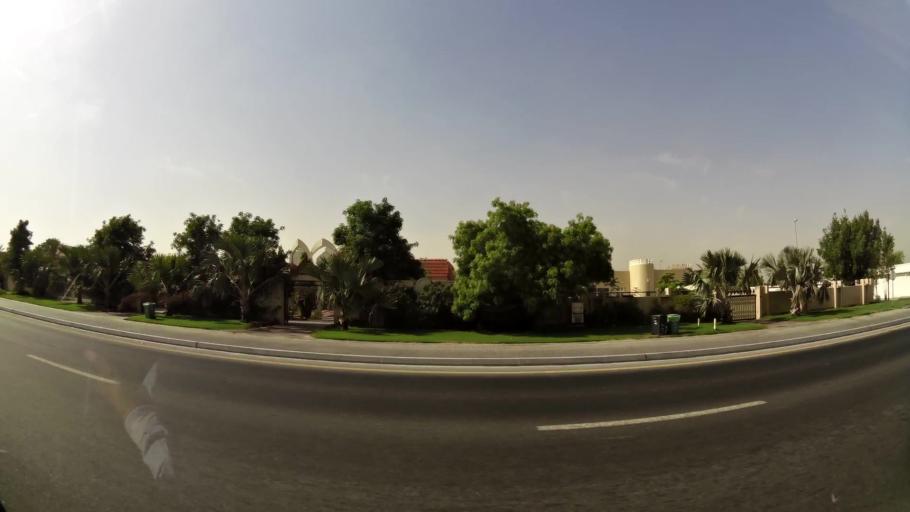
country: AE
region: Ash Shariqah
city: Sharjah
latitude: 25.2524
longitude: 55.4127
